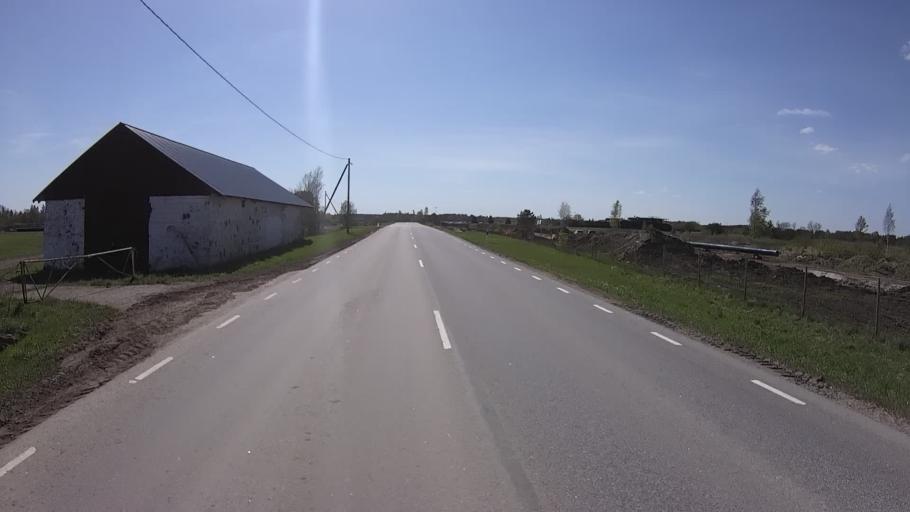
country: EE
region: Harju
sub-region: Keila linn
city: Keila
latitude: 59.3202
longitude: 24.3219
